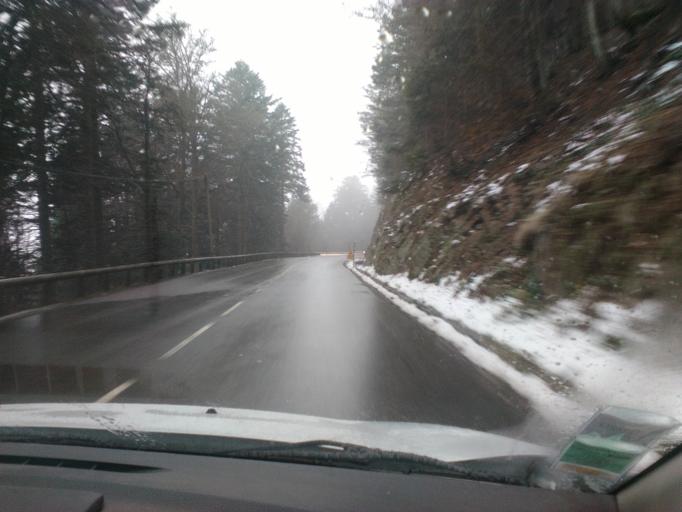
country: FR
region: Lorraine
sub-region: Departement des Vosges
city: Xonrupt-Longemer
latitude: 48.0635
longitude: 6.9894
